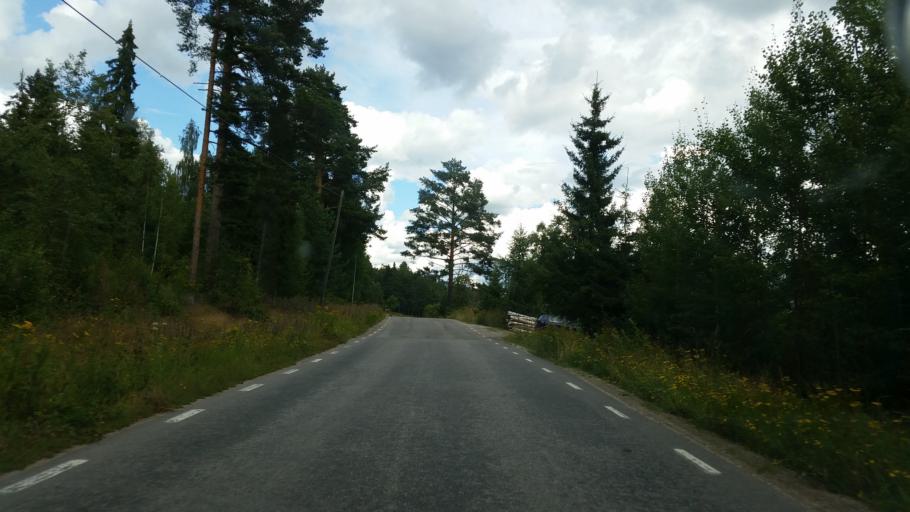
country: SE
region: Gaevleborg
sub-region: Hudiksvalls Kommun
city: Delsbo
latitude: 61.9174
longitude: 16.5989
